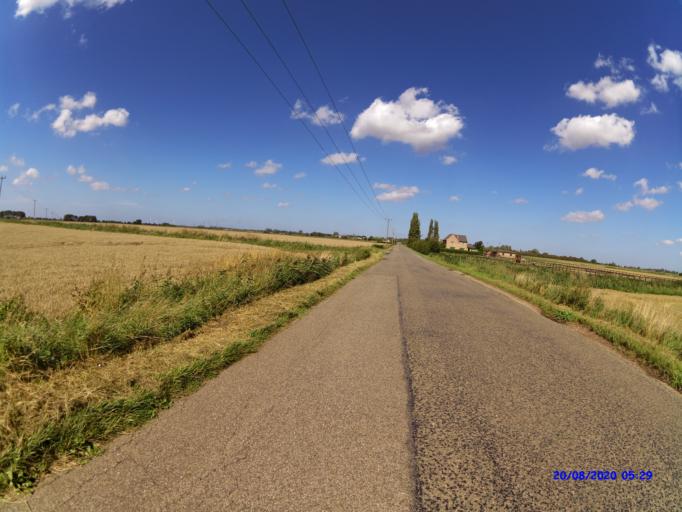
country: GB
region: England
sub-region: Cambridgeshire
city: Whittlesey
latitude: 52.5365
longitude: -0.1071
